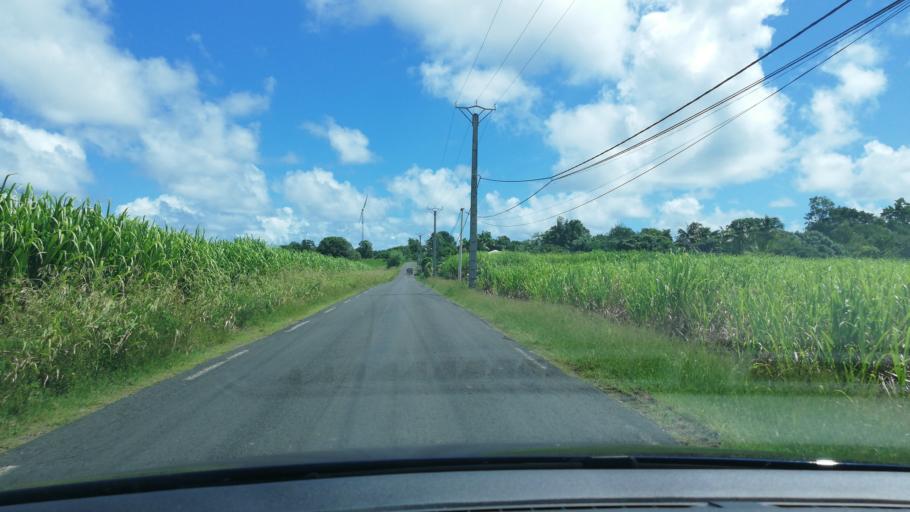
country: GP
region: Guadeloupe
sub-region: Guadeloupe
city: Petit-Canal
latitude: 16.3804
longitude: -61.4347
